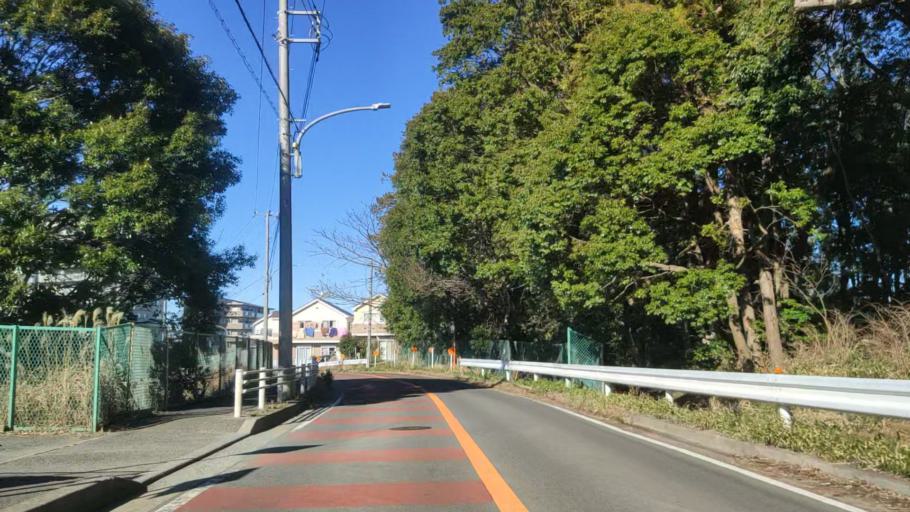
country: JP
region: Kanagawa
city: Minami-rinkan
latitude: 35.5057
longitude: 139.5348
